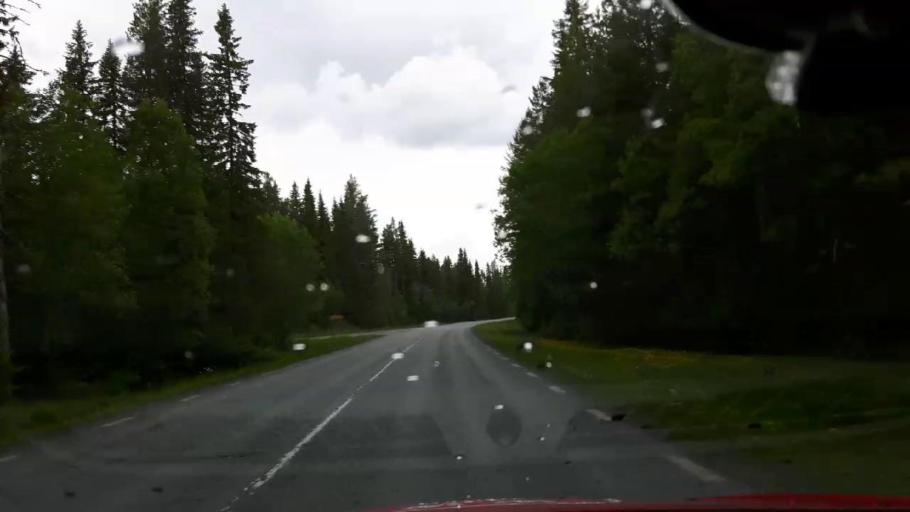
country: SE
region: Jaemtland
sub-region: Krokoms Kommun
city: Krokom
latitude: 63.4107
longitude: 14.2410
